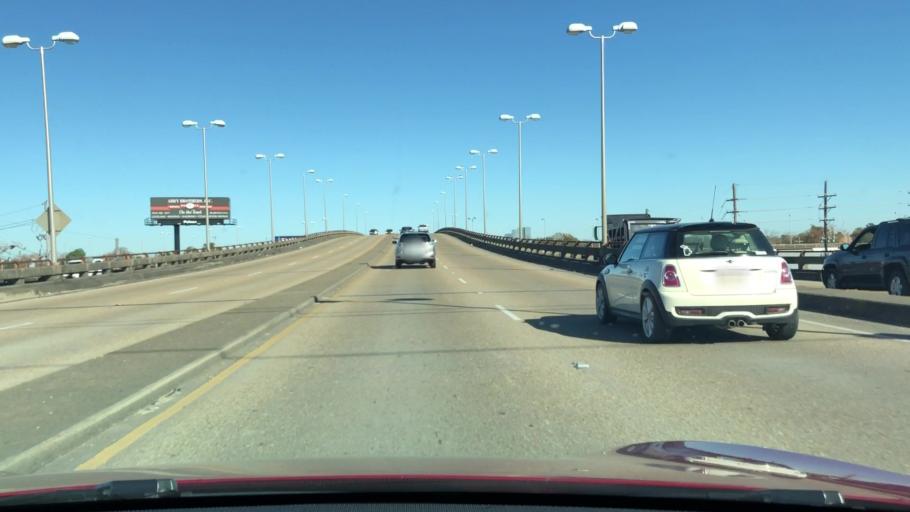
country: US
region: Louisiana
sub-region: Jefferson Parish
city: Jefferson
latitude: 29.9726
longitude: -90.1564
